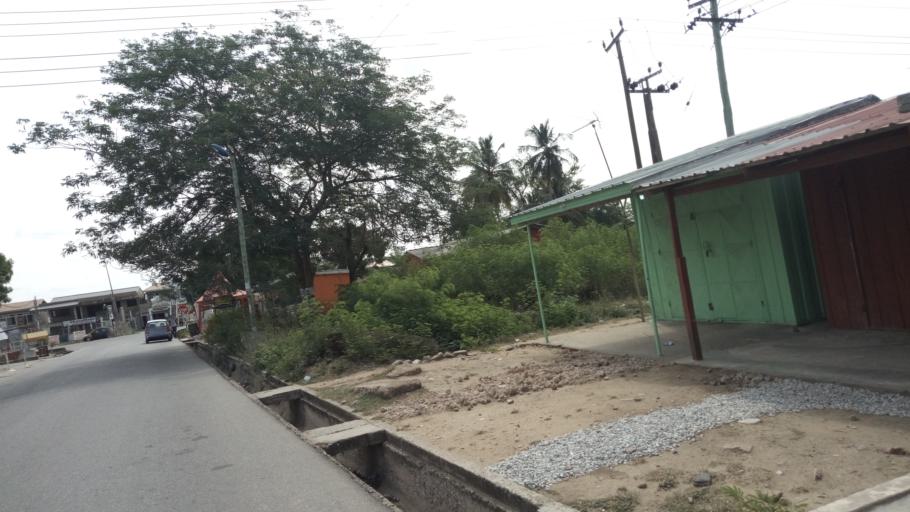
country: GH
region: Central
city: Winneba
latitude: 5.3717
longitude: -0.6398
